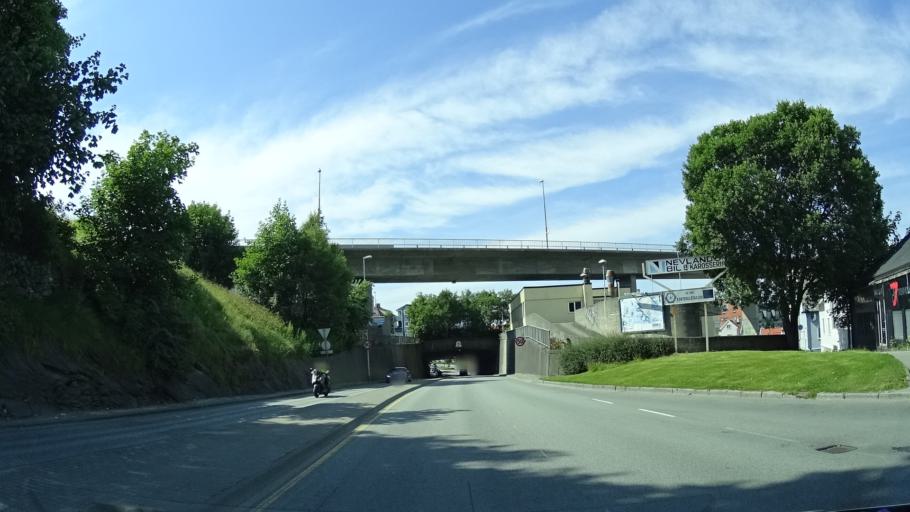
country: NO
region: Rogaland
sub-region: Stavanger
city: Stavanger
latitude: 58.9695
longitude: 5.7496
